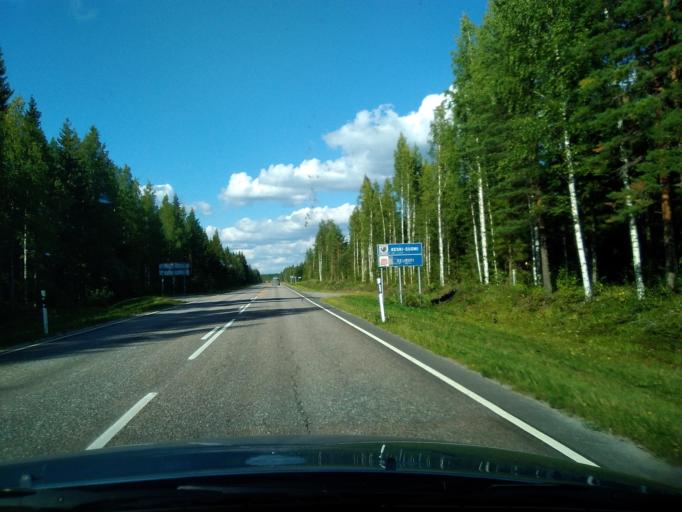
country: FI
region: Pirkanmaa
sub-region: Ylae-Pirkanmaa
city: Maenttae
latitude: 62.0402
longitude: 24.7106
